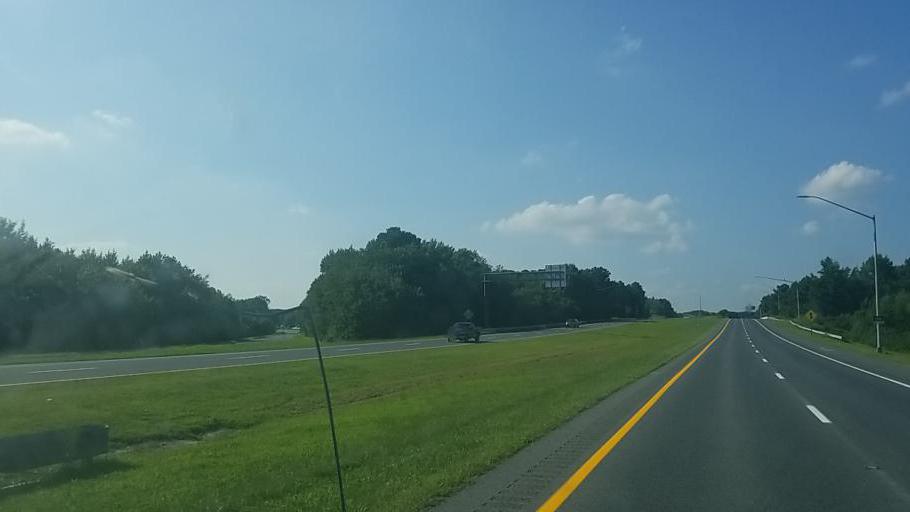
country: US
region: Maryland
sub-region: Worcester County
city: Berlin
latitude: 38.3393
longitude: -75.2126
